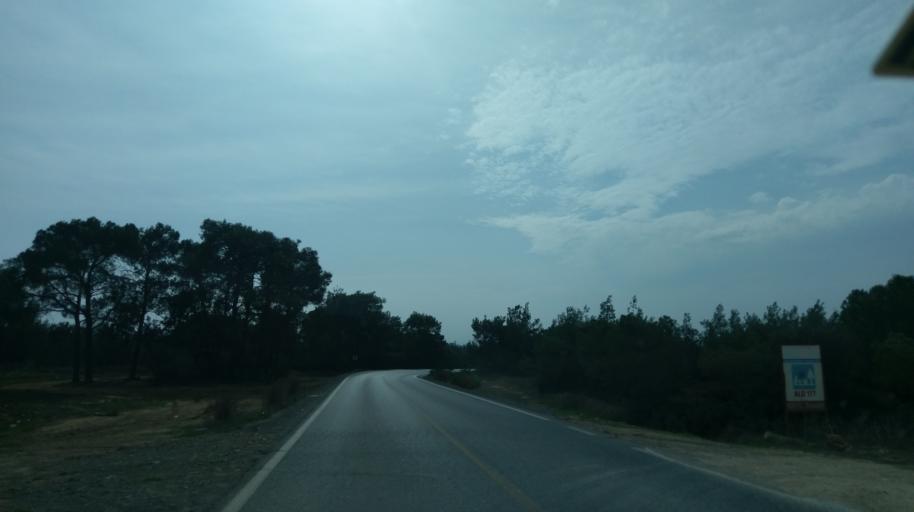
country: CY
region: Lefkosia
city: Morfou
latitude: 35.2879
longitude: 33.0414
